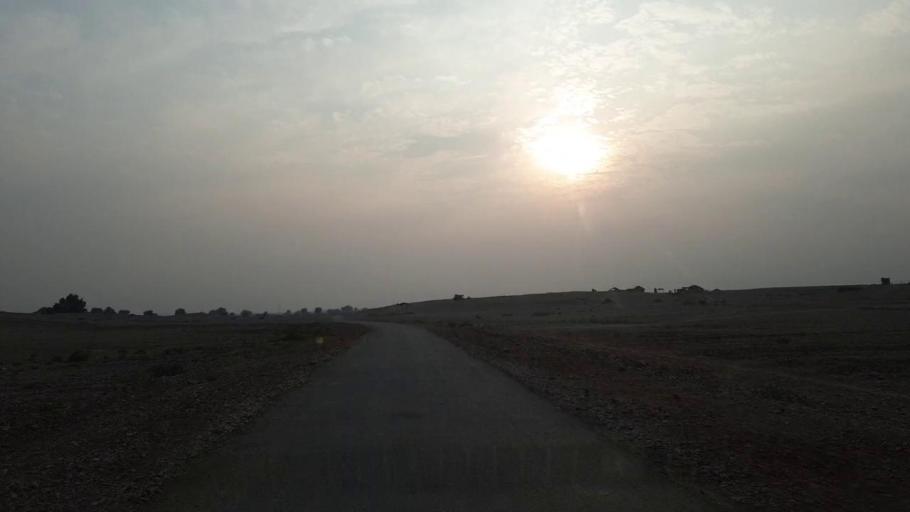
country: PK
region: Sindh
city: Sann
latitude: 26.1618
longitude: 68.0052
